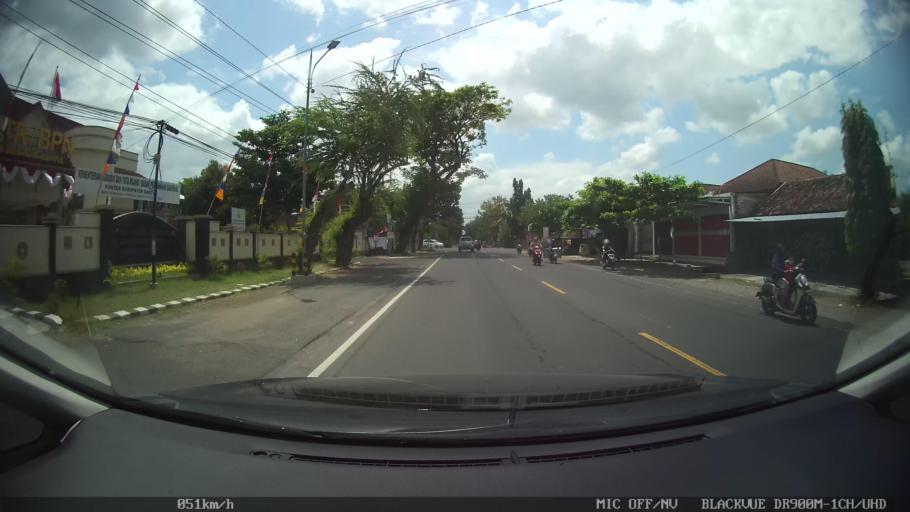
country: ID
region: Daerah Istimewa Yogyakarta
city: Bantul
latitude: -7.8957
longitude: 110.3466
